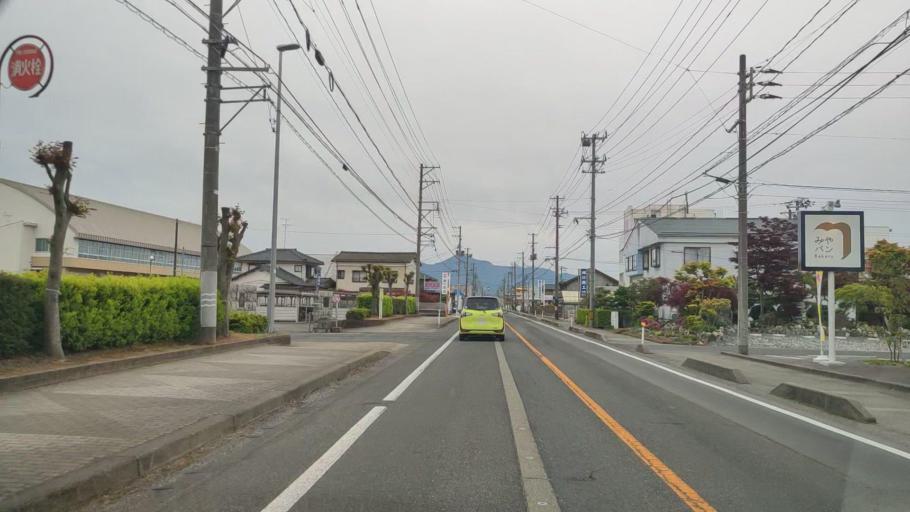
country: JP
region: Niigata
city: Gosen
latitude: 37.7330
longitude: 139.1768
